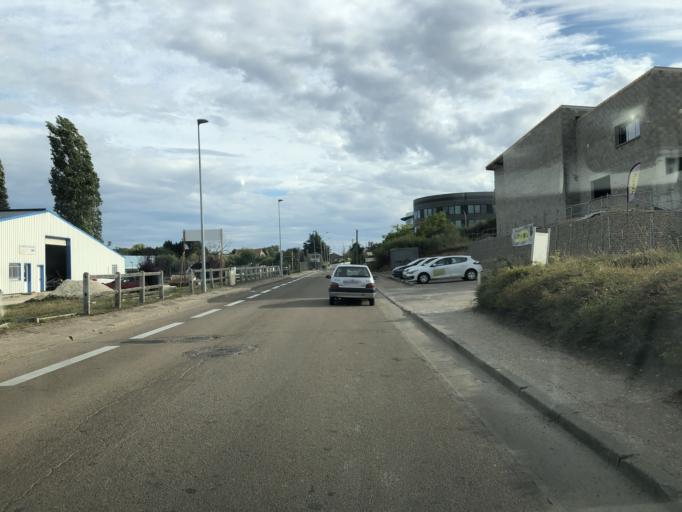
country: FR
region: Bourgogne
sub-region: Departement de l'Yonne
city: Auxerre
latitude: 47.8150
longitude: 3.5765
